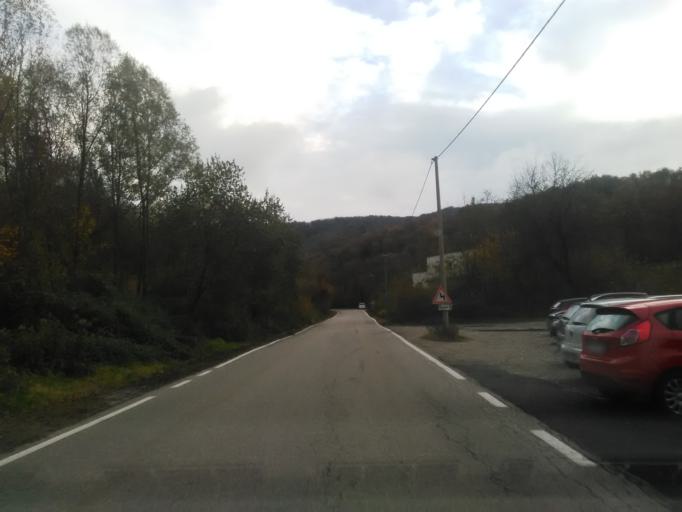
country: IT
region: Piedmont
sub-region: Provincia di Novara
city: Pogno
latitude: 45.7502
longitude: 8.3814
